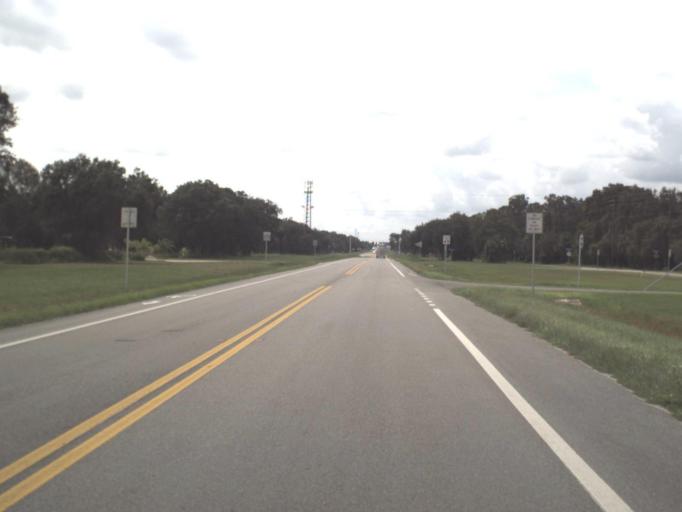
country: US
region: Florida
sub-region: Hendry County
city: LaBelle
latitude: 26.7812
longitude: -81.4375
